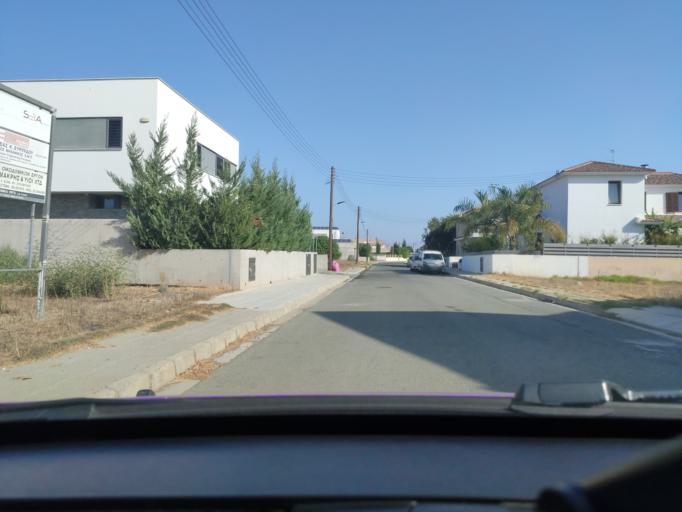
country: CY
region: Lefkosia
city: Tseri
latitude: 35.1056
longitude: 33.3520
